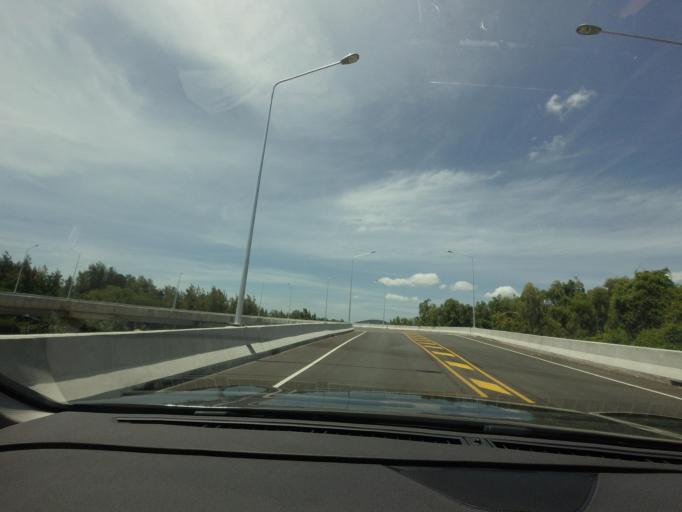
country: TH
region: Prachuap Khiri Khan
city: Hua Hin
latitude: 12.4938
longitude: 99.9723
